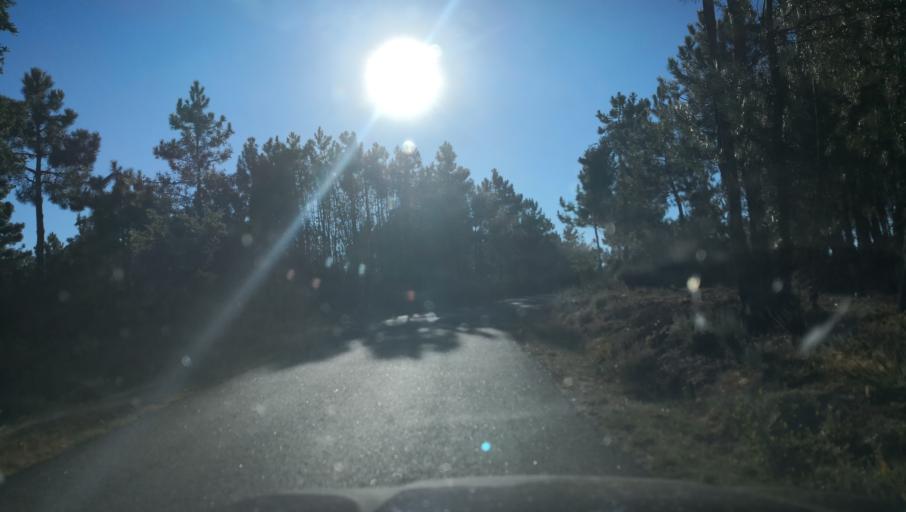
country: PT
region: Vila Real
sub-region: Sabrosa
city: Sabrosa
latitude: 41.3258
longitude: -7.6201
